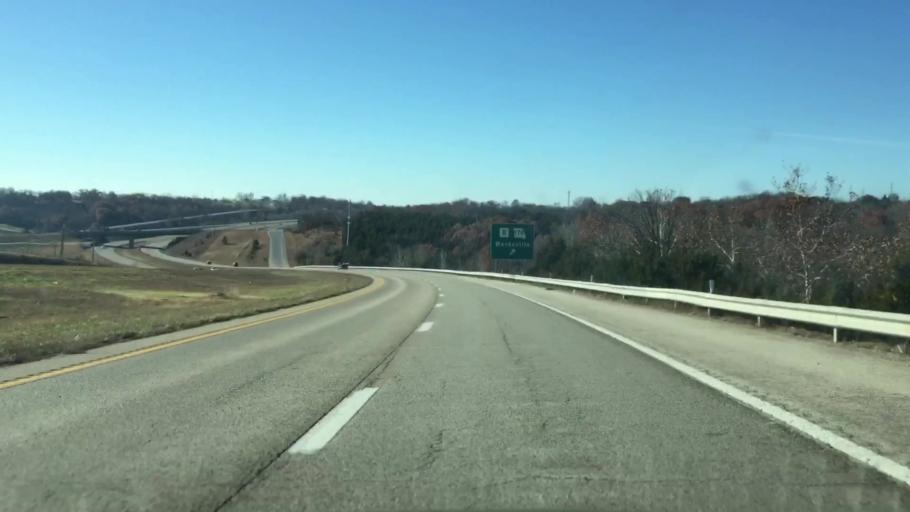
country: US
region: Missouri
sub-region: Cole County
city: Jefferson City
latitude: 38.5465
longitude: -92.2072
